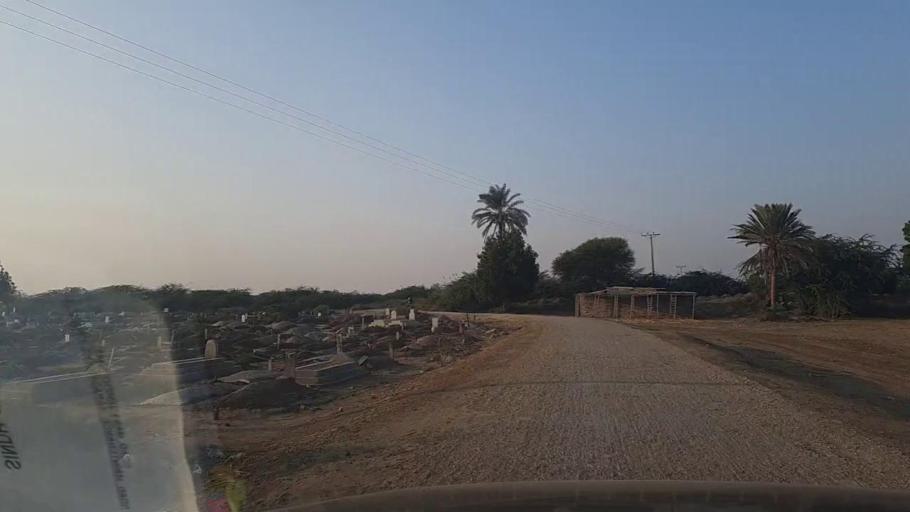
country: PK
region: Sindh
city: Keti Bandar
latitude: 24.3080
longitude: 67.6027
